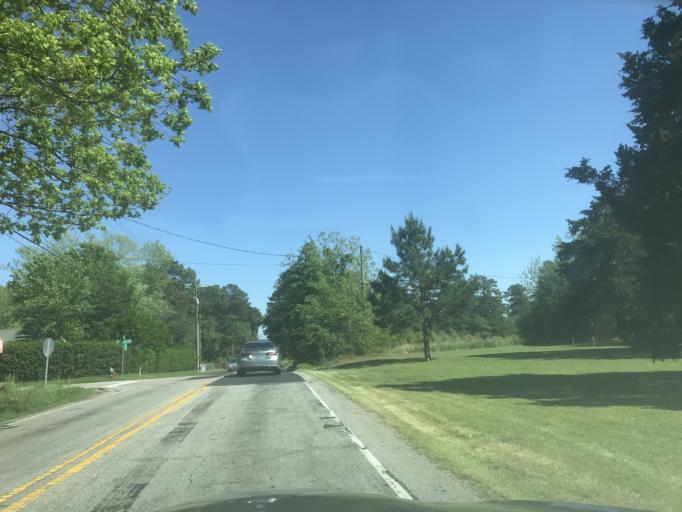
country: US
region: North Carolina
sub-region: Wake County
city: Raleigh
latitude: 35.7402
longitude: -78.6691
